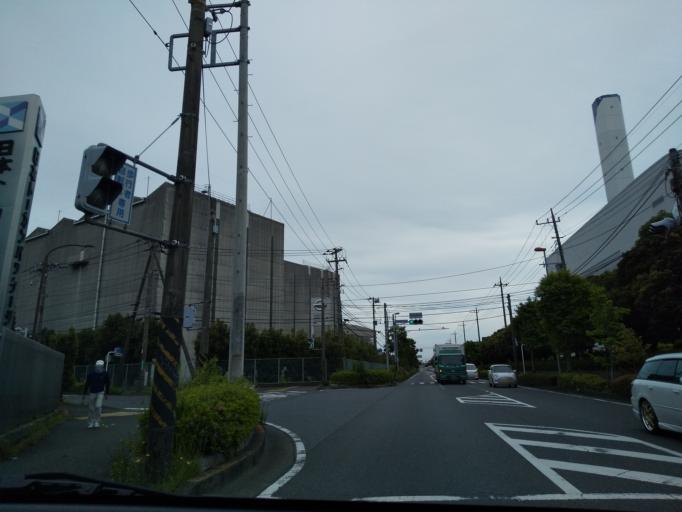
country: JP
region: Kanagawa
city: Zama
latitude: 35.5318
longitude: 139.3941
